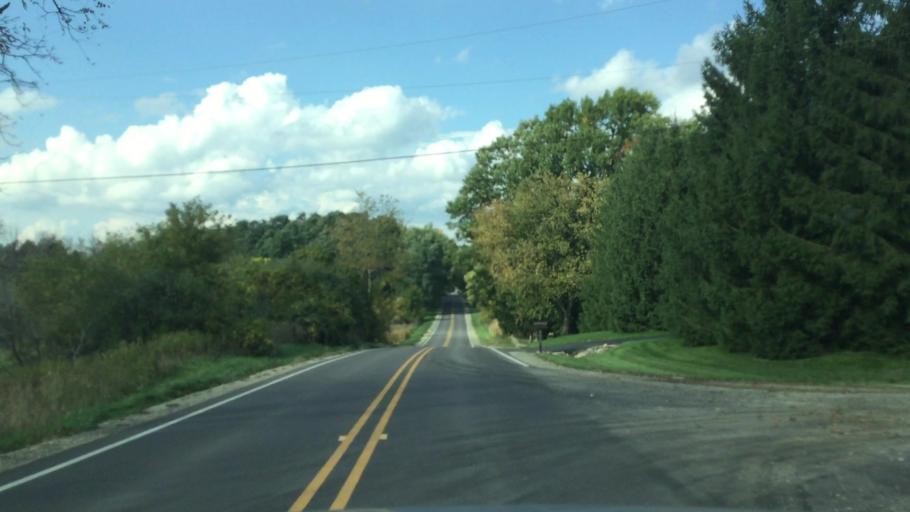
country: US
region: Michigan
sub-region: Genesee County
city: Fenton
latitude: 42.7023
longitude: -83.7030
